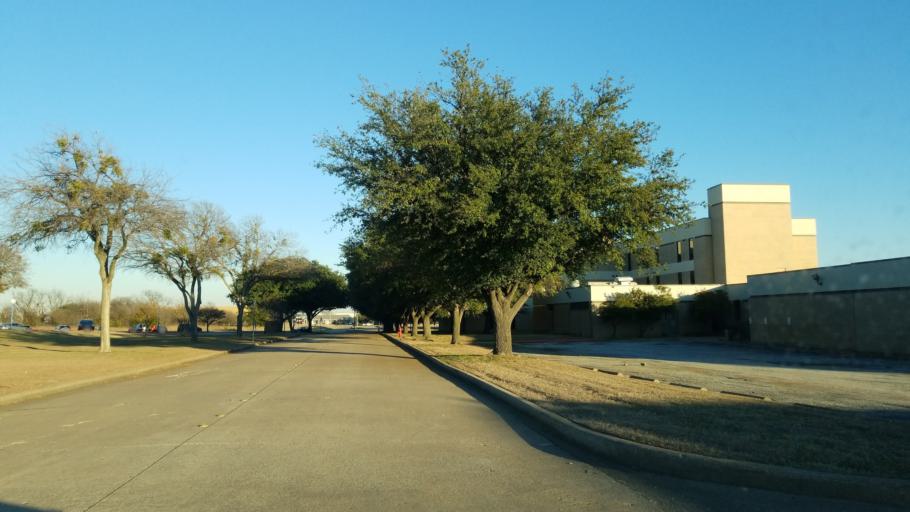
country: US
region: Texas
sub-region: Dallas County
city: Grand Prairie
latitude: 32.7337
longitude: -97.0503
